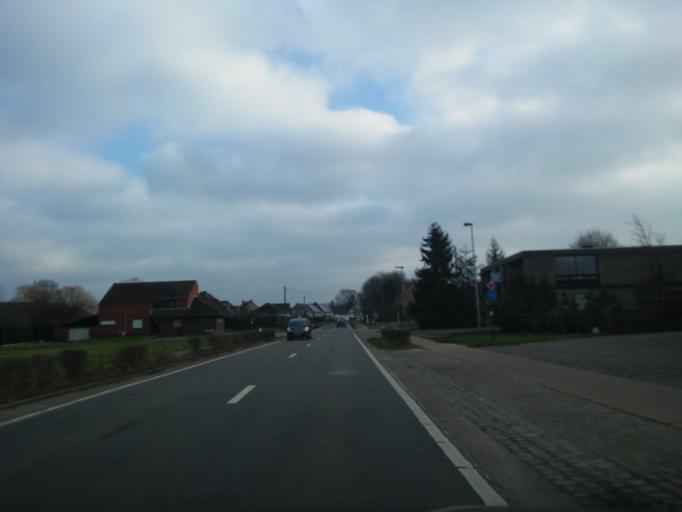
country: BE
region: Flanders
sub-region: Provincie Antwerpen
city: Herselt
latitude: 51.0529
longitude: 4.8854
